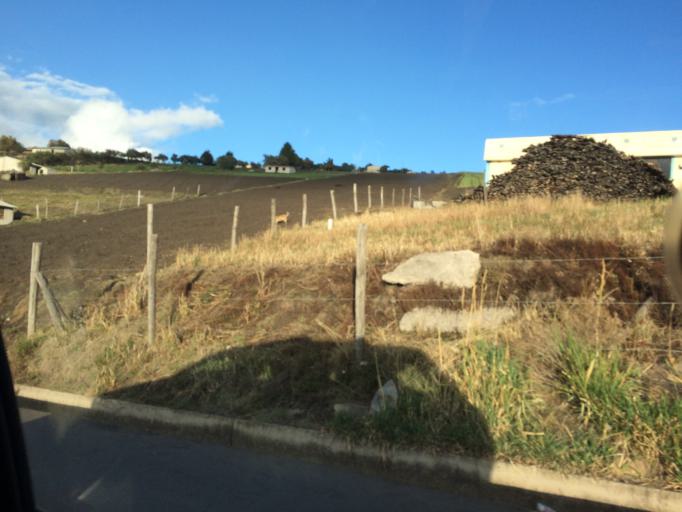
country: EC
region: Chimborazo
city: Alausi
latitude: -2.1399
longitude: -78.7190
